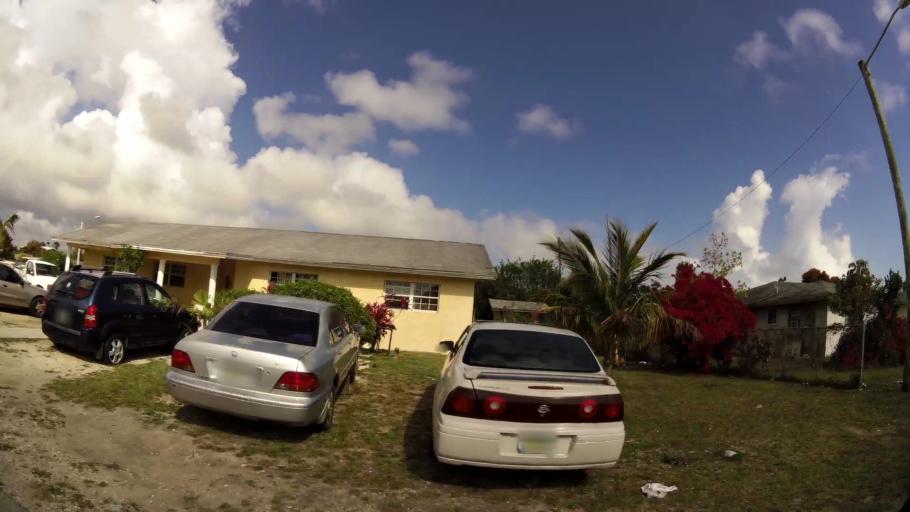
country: BS
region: Freeport
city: Lucaya
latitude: 26.5281
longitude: -78.6808
